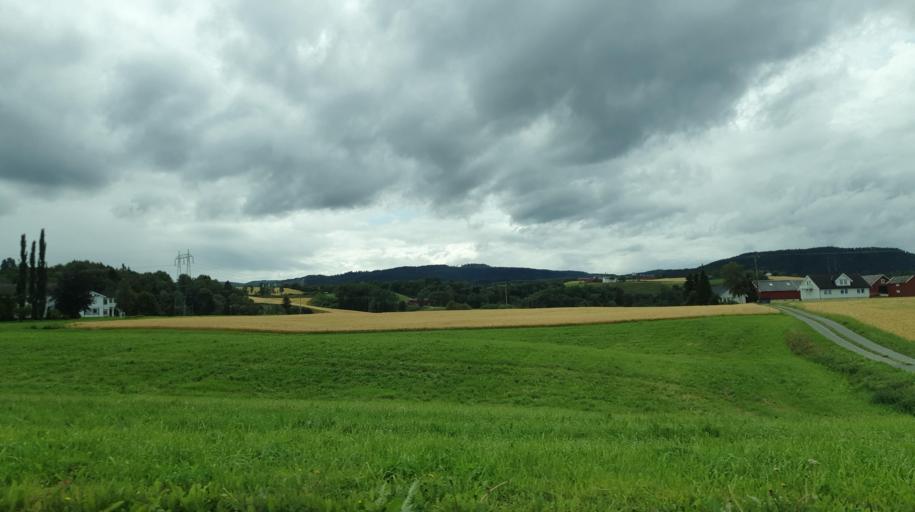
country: NO
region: Nord-Trondelag
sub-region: Stjordal
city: Stjordalshalsen
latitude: 63.4344
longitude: 10.9467
